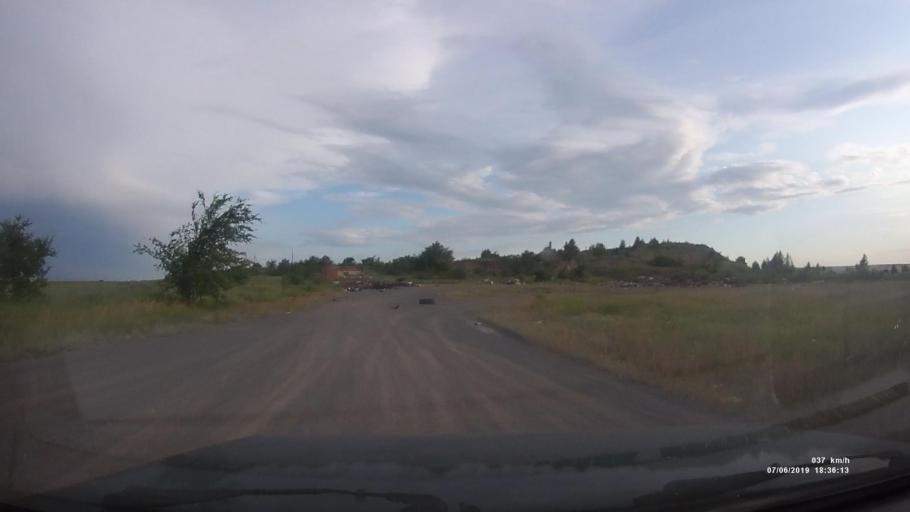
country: RU
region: Rostov
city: Staraya Stanitsa
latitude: 48.2520
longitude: 40.3538
